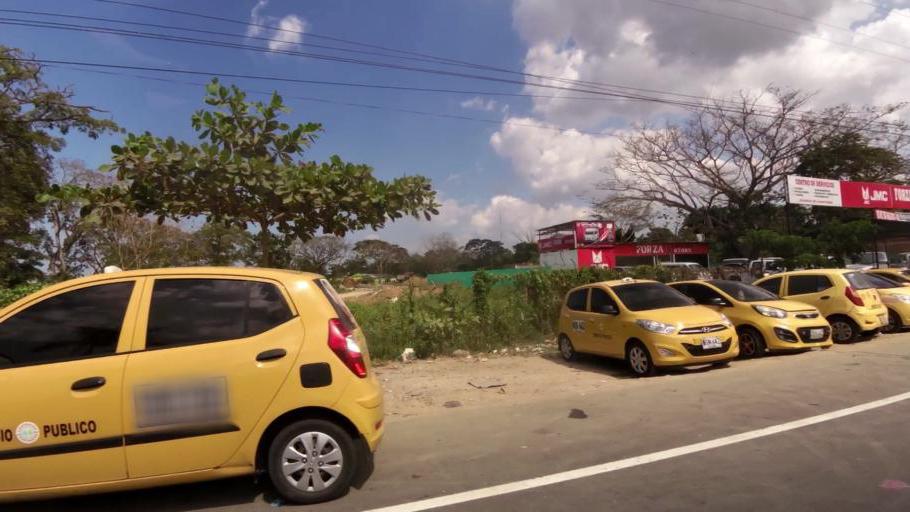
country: CO
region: Bolivar
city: Cartagena
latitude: 10.3762
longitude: -75.4600
